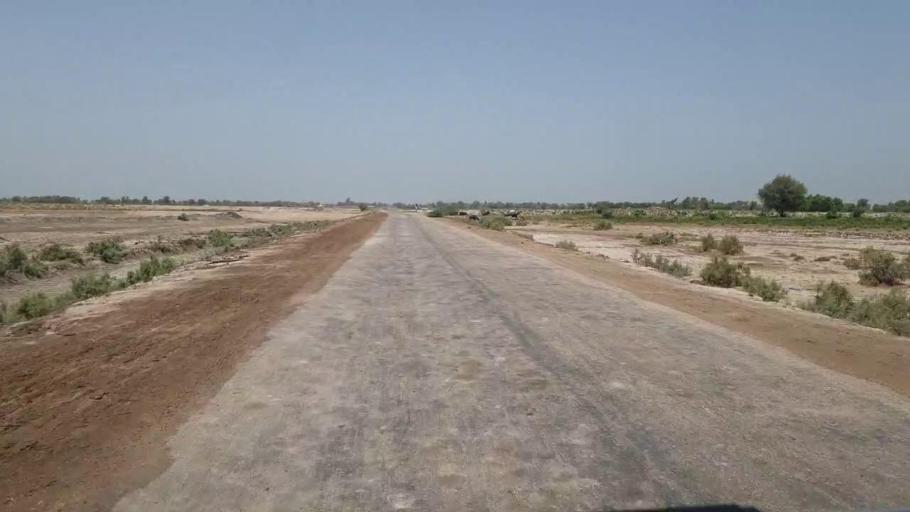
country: PK
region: Sindh
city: Nawabshah
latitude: 26.3637
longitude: 68.4086
